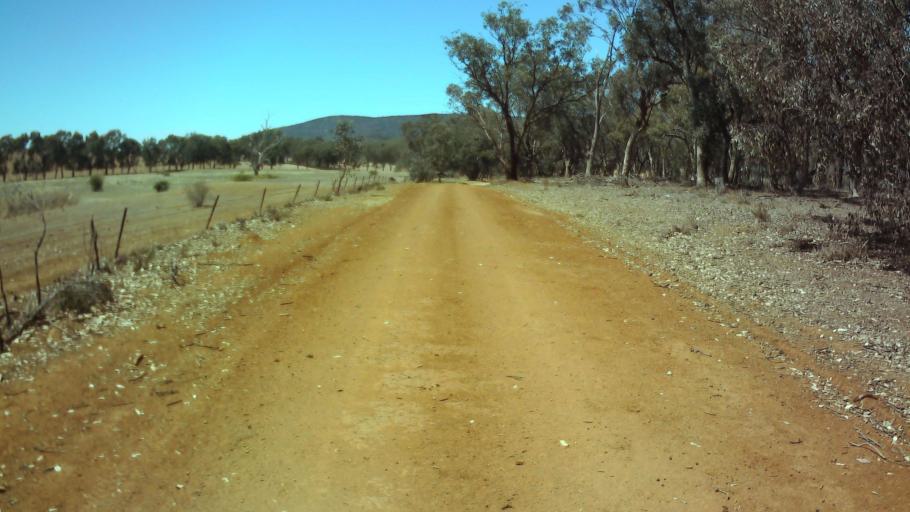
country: AU
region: New South Wales
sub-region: Weddin
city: Grenfell
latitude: -33.9518
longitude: 148.0846
